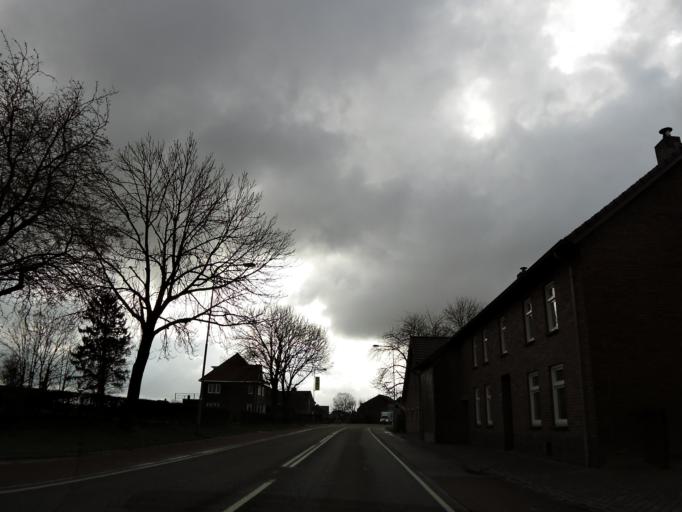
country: NL
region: Limburg
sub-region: Gemeente Maastricht
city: Heer
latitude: 50.8031
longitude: 5.7610
